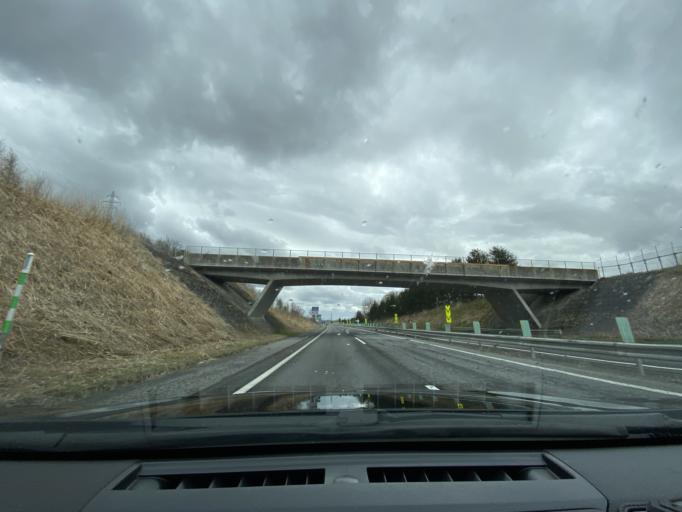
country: JP
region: Hokkaido
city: Takikawa
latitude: 43.5347
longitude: 141.9304
